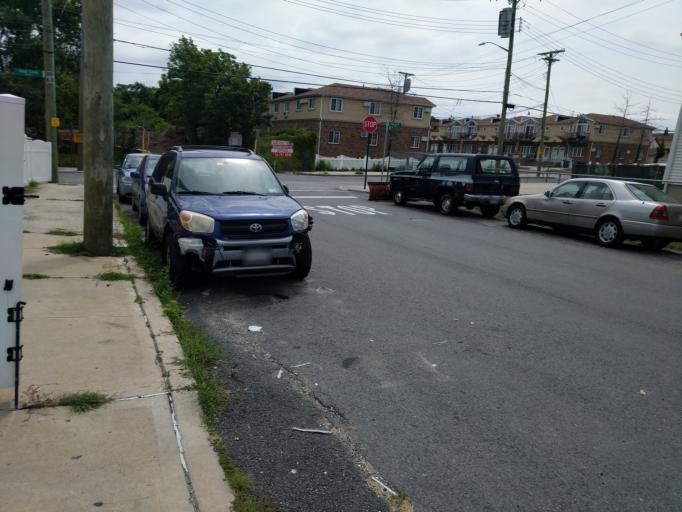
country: US
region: New York
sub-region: Nassau County
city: South Valley Stream
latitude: 40.6557
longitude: -73.7268
